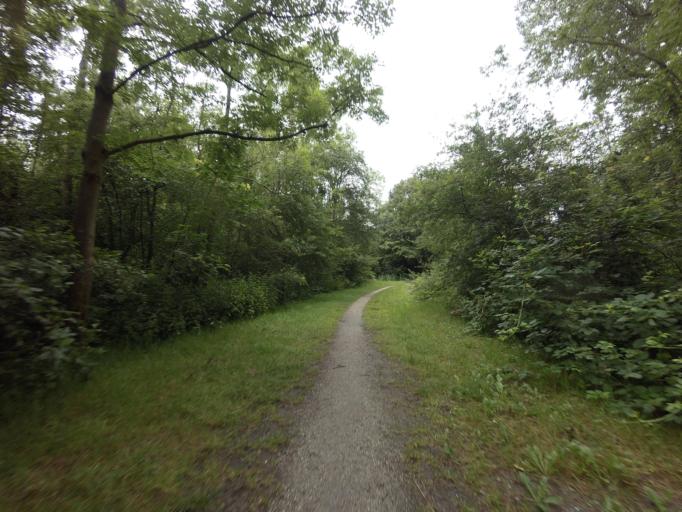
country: NL
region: North Holland
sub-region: Gemeente Velsen
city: Velsen-Zuid
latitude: 52.4206
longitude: 4.7025
